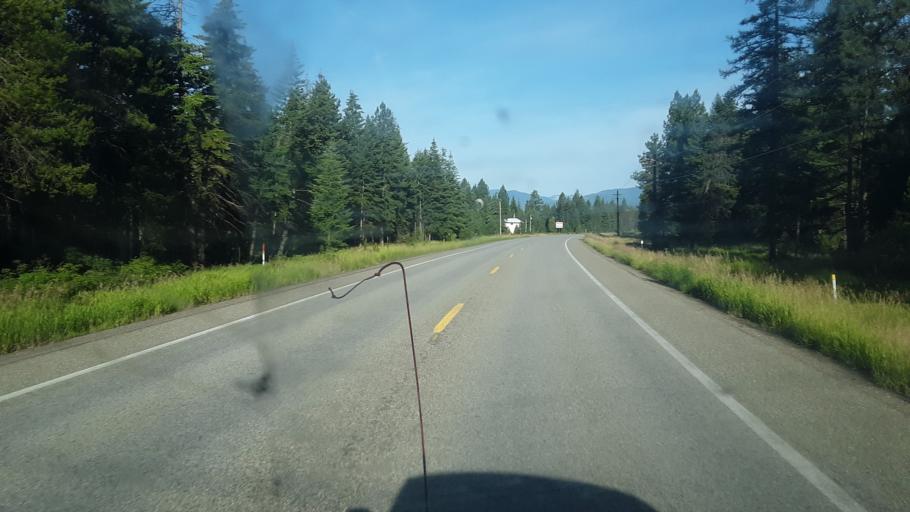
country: US
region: Idaho
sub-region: Boundary County
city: Bonners Ferry
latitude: 48.7267
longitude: -116.2075
